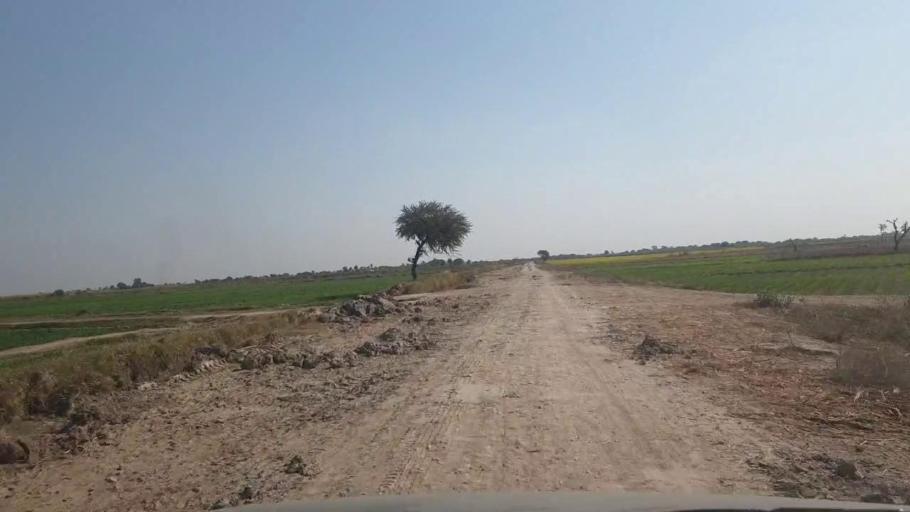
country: PK
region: Sindh
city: Chambar
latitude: 25.3205
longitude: 68.8699
